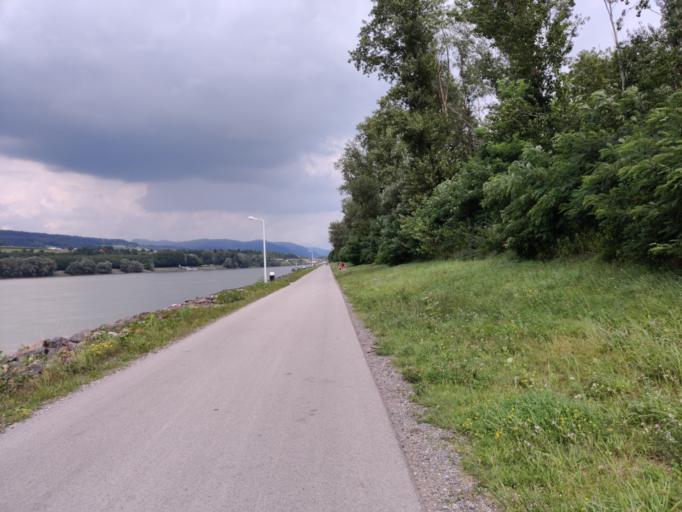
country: AT
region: Lower Austria
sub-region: Politischer Bezirk Melk
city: Melk
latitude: 48.2281
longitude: 15.3196
